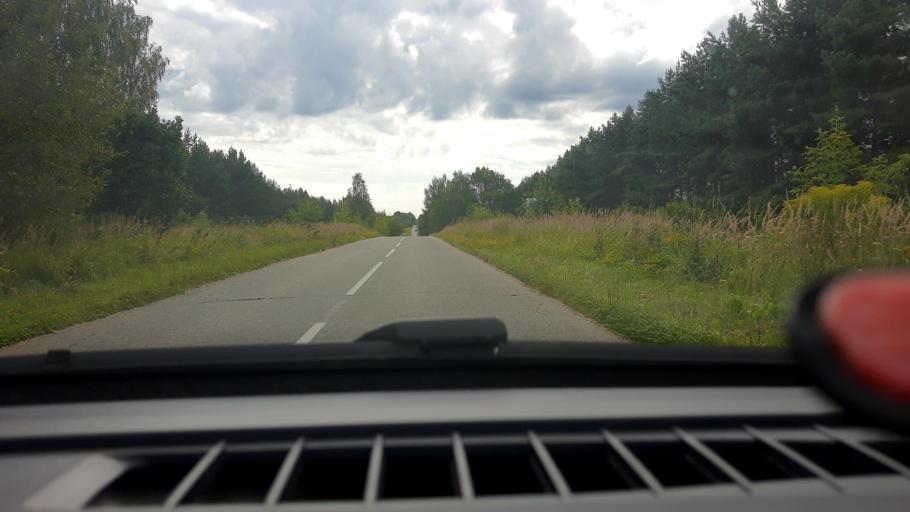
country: RU
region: Nizjnij Novgorod
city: Burevestnik
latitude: 56.0486
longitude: 43.7037
